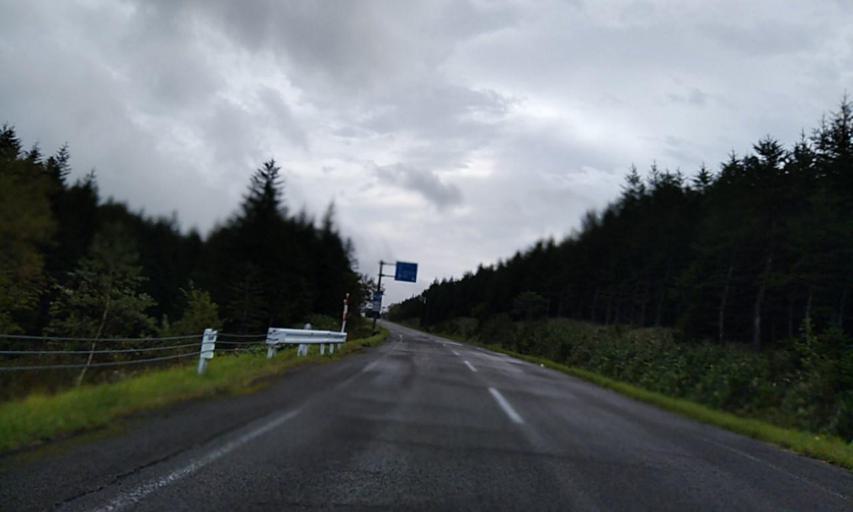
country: JP
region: Hokkaido
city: Abashiri
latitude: 43.6147
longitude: 144.5867
